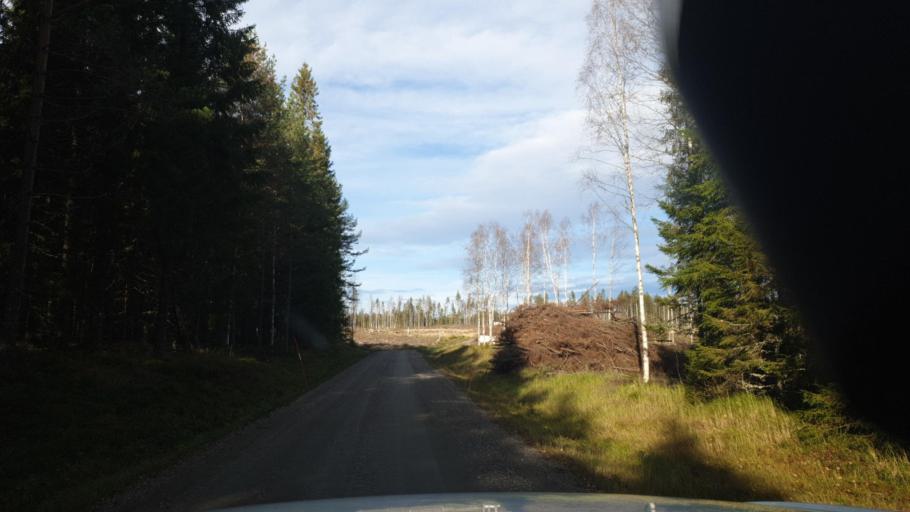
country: SE
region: Vaermland
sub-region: Eda Kommun
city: Charlottenberg
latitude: 60.0511
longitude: 12.5238
